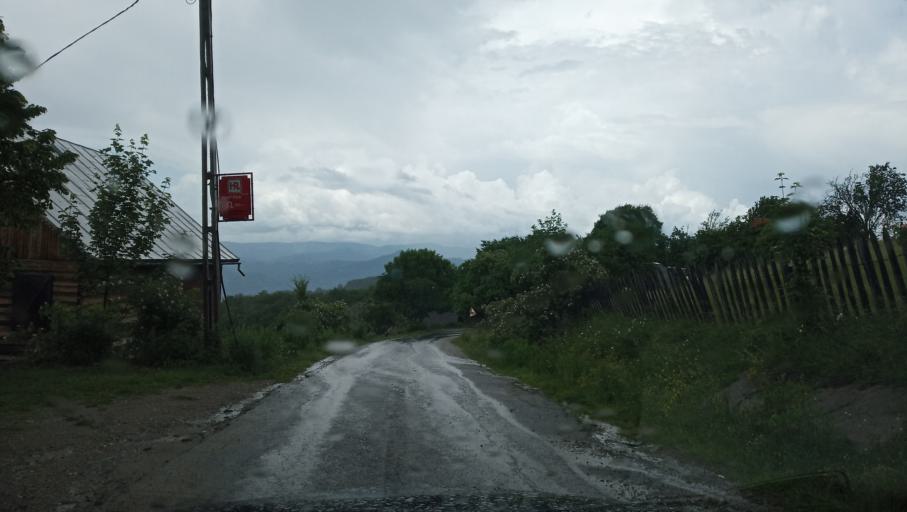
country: RO
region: Hunedoara
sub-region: Oras Petrila
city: Petrila
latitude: 45.3898
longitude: 23.4374
